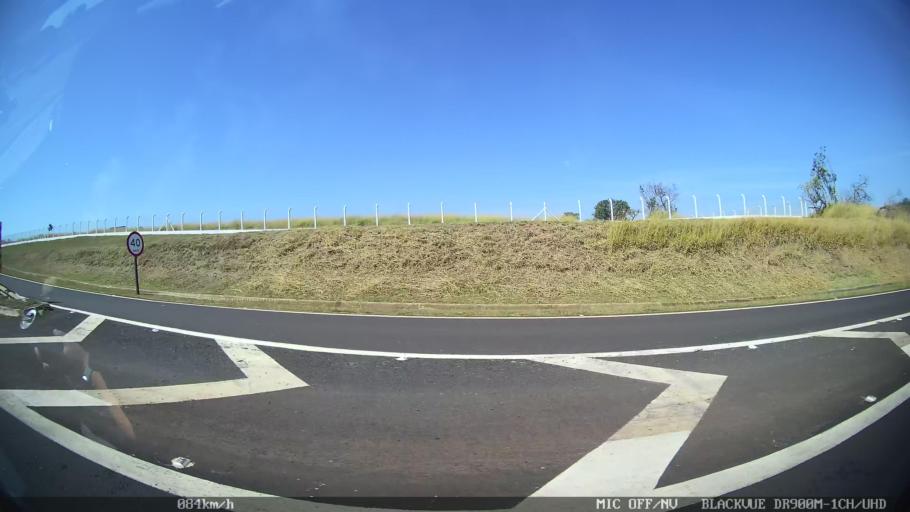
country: BR
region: Sao Paulo
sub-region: Batatais
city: Batatais
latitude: -20.8717
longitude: -47.6030
